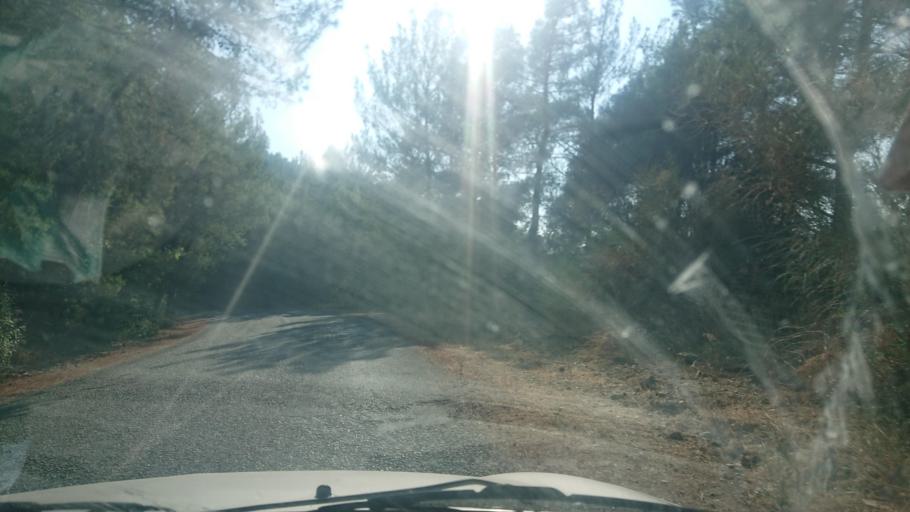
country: TR
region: Aydin
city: Atburgazi
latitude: 37.6908
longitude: 27.1455
